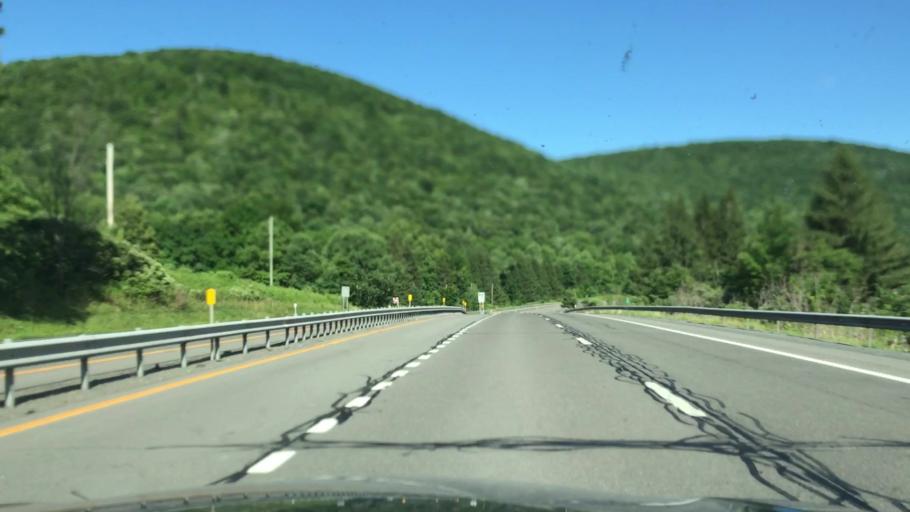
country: US
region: New York
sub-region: Delaware County
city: Hancock
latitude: 41.9965
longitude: -75.3460
